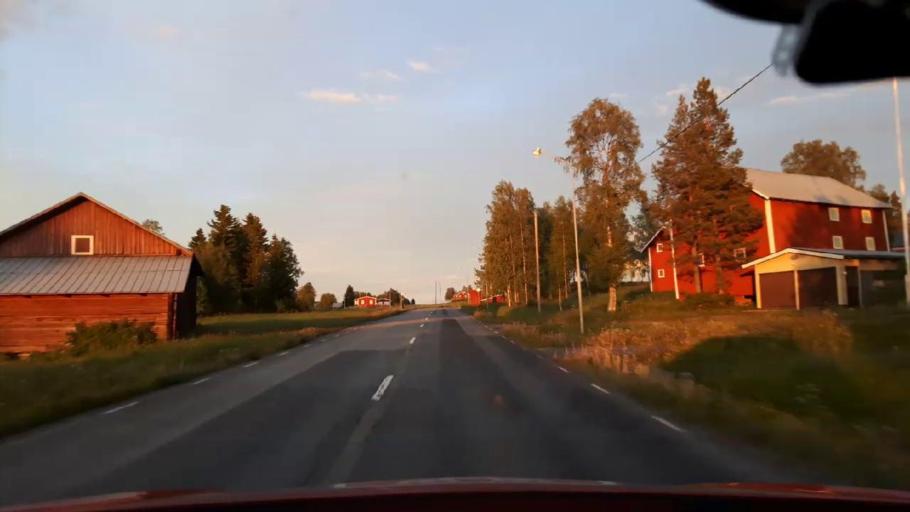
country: SE
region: Jaemtland
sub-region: OEstersunds Kommun
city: Ostersund
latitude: 63.1263
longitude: 14.6870
